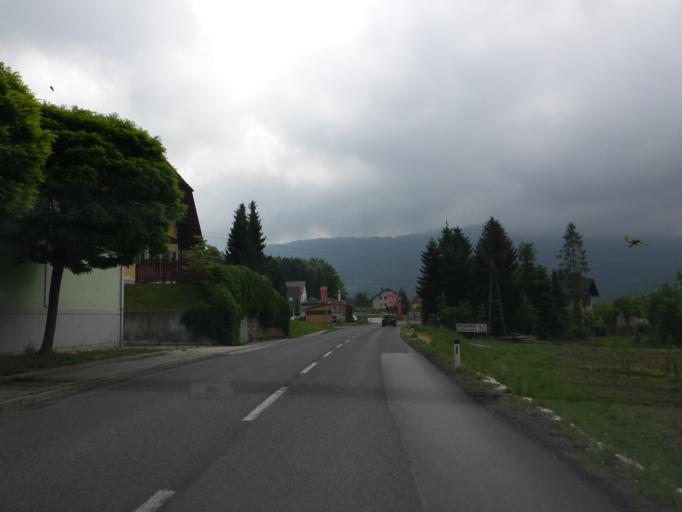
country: AT
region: Styria
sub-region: Politischer Bezirk Weiz
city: Floing
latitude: 47.2506
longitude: 15.7273
